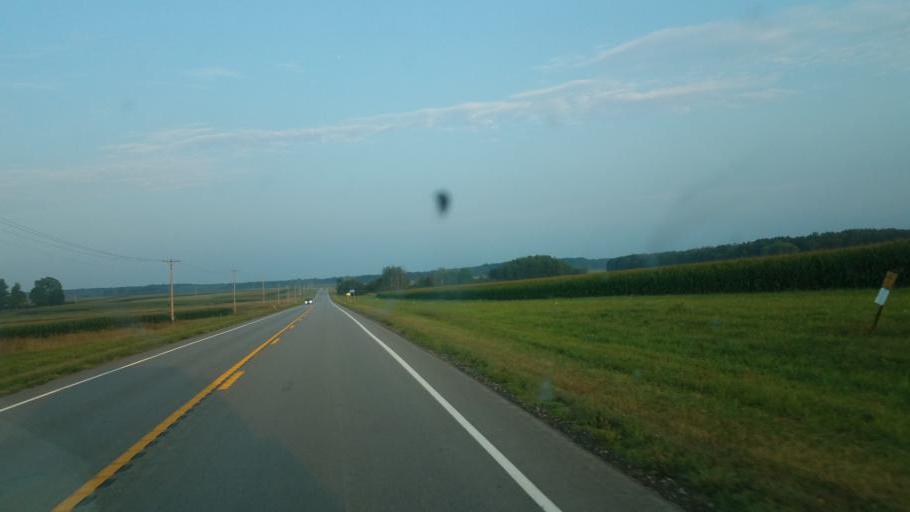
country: US
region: Pennsylvania
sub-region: Crawford County
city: Linesville
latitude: 41.6059
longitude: -80.4070
